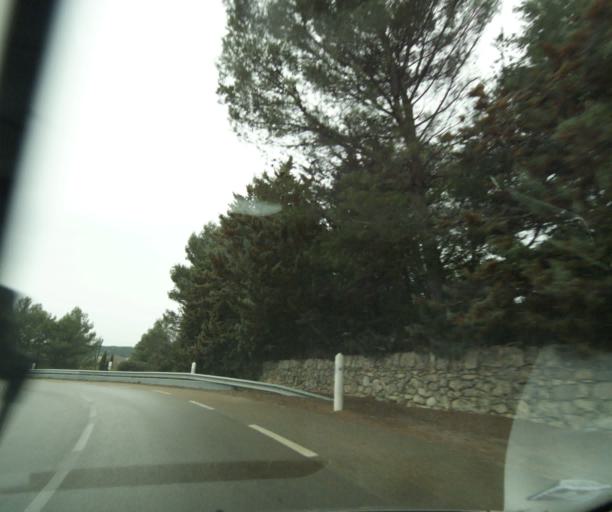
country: FR
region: Provence-Alpes-Cote d'Azur
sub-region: Departement des Bouches-du-Rhone
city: Rognes
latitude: 43.6621
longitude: 5.3662
